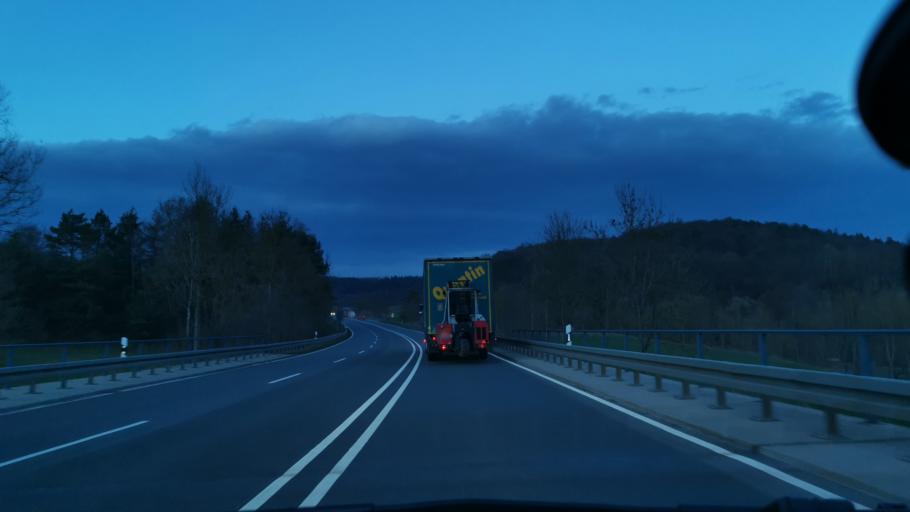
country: DE
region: Hesse
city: Bebra
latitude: 51.0161
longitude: 9.8223
